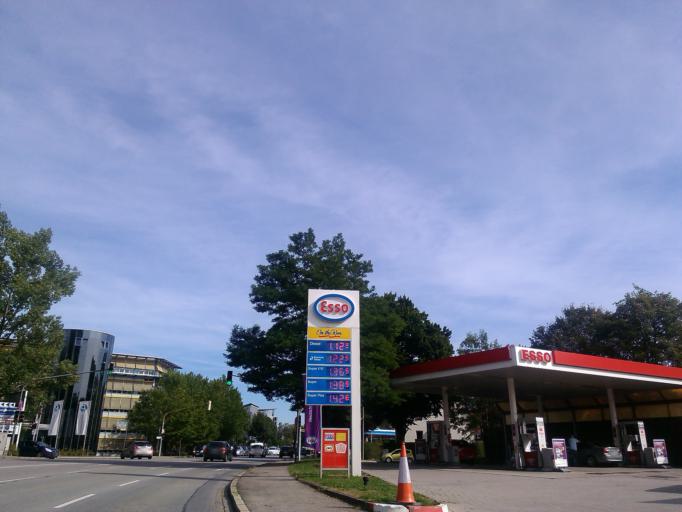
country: DE
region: Bavaria
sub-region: Upper Bavaria
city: Starnberg
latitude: 48.0023
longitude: 11.3484
